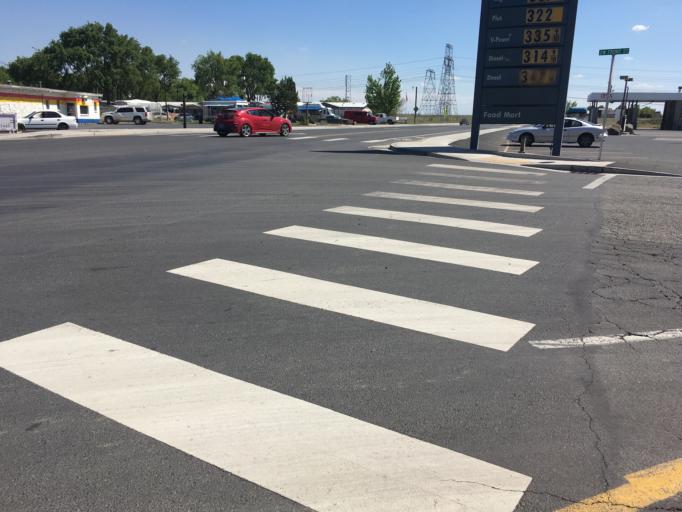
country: US
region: Oregon
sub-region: Morrow County
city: Boardman
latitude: 45.8367
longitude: -119.7013
